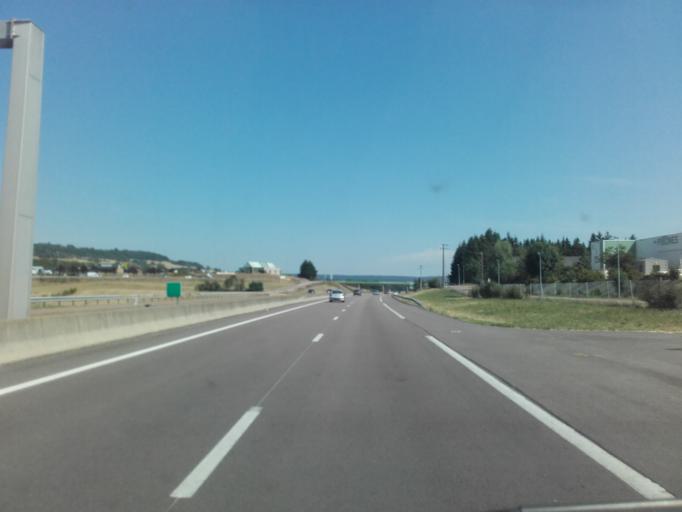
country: FR
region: Bourgogne
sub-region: Departement de la Cote-d'Or
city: Pouilly-en-Auxois
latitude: 47.2509
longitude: 4.5610
